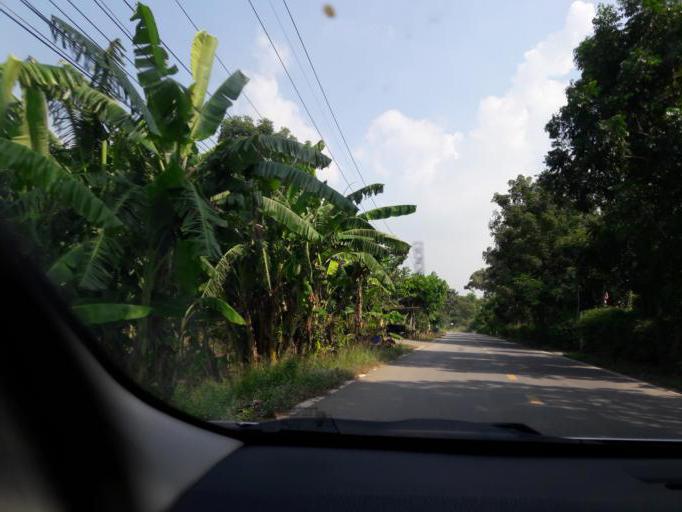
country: TH
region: Ang Thong
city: Ang Thong
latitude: 14.5449
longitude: 100.4099
